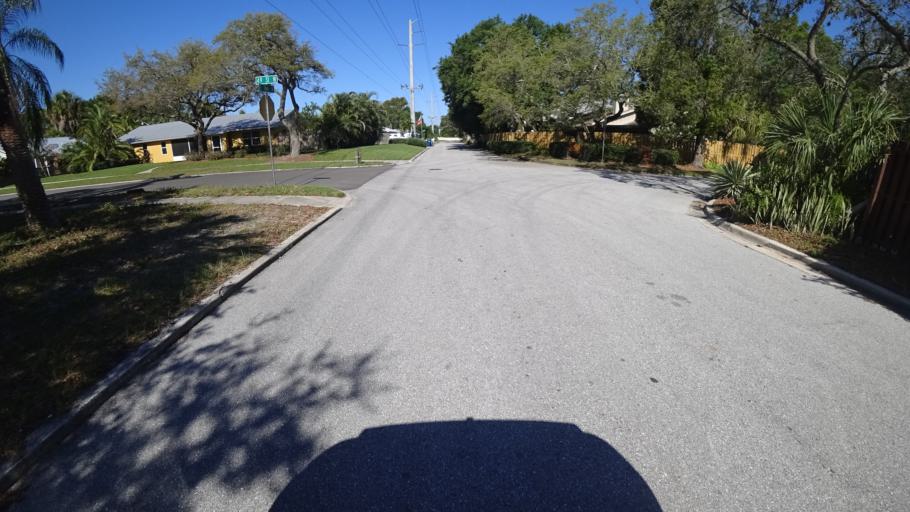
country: US
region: Florida
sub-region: Manatee County
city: West Bradenton
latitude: 27.4995
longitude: -82.6100
